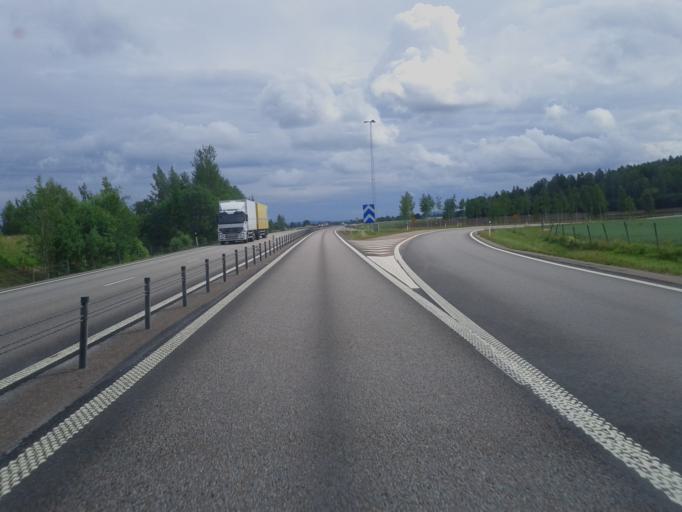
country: SE
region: Dalarna
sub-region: Borlange Kommun
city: Ornas
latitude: 60.4119
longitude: 15.5874
